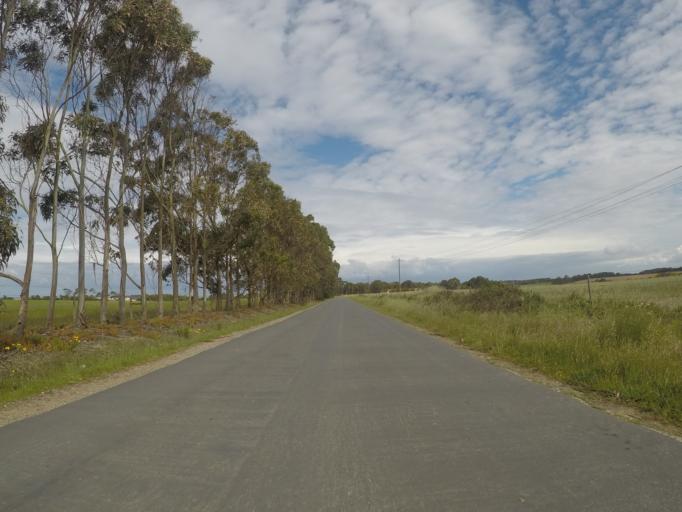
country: PT
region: Beja
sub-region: Odemira
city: Sao Teotonio
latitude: 37.4923
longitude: -8.7827
